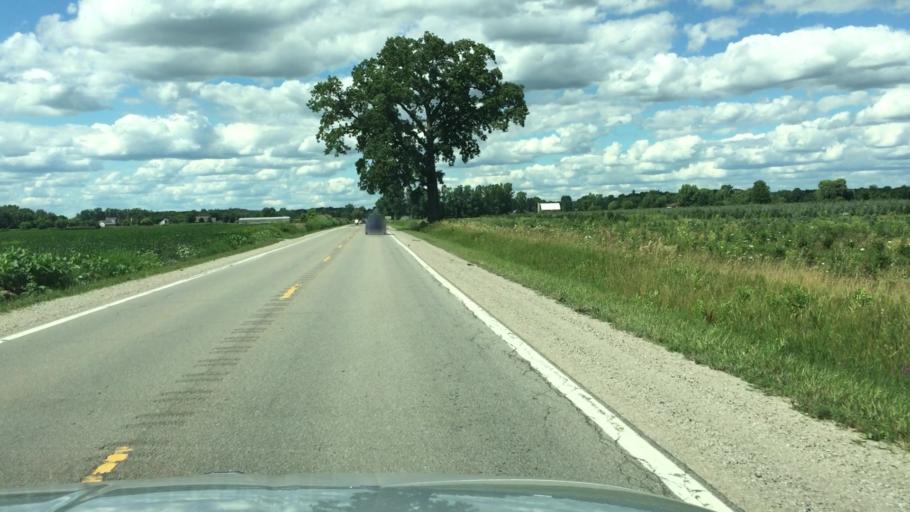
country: US
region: Michigan
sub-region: Macomb County
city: Romeo
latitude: 42.8409
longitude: -82.9640
